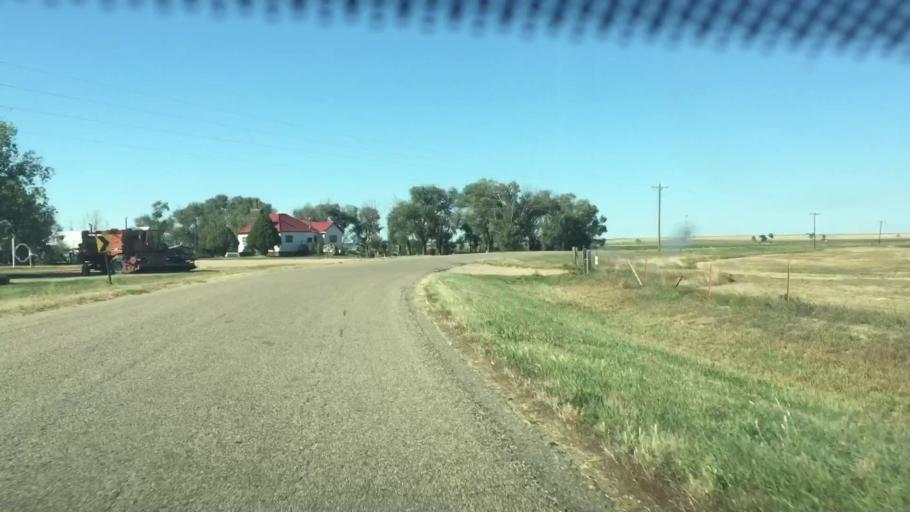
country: US
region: Colorado
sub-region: Prowers County
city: Lamar
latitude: 38.1000
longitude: -102.5209
